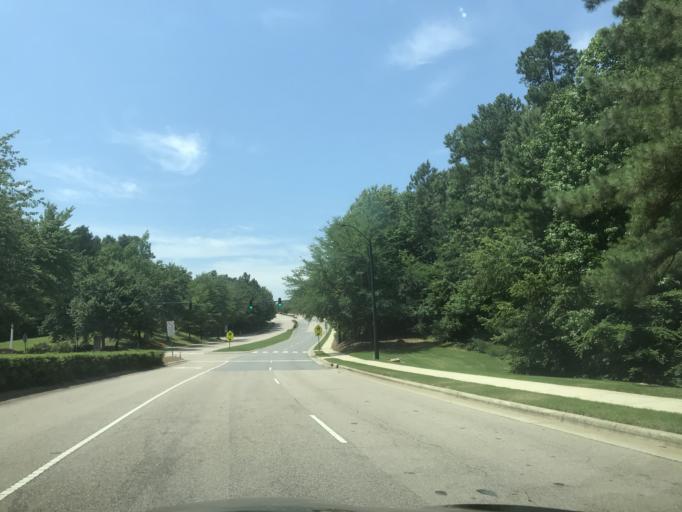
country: US
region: North Carolina
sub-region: Wake County
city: Wake Forest
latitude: 35.9459
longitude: -78.5656
